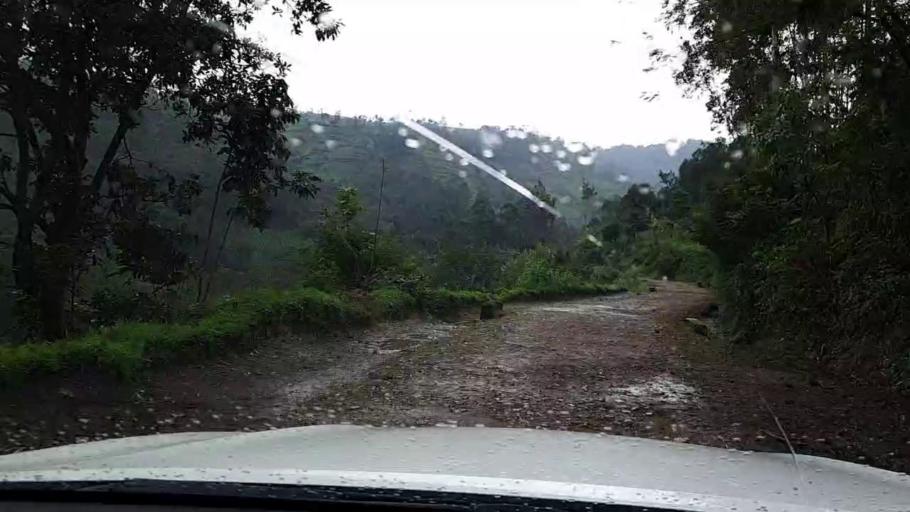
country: RW
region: Western Province
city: Cyangugu
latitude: -2.5354
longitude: 29.0424
